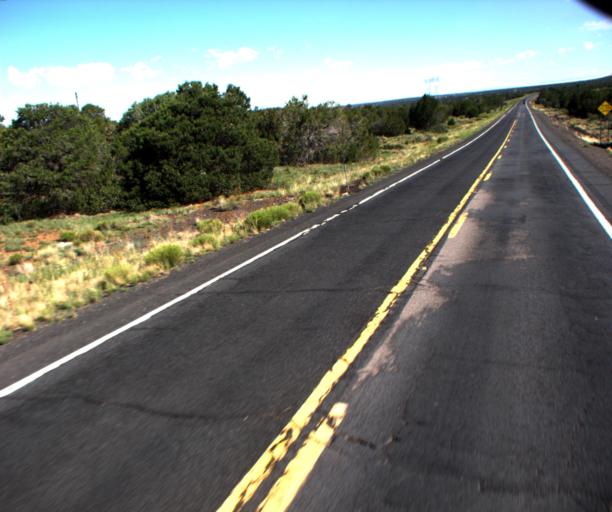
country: US
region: Arizona
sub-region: Coconino County
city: Williams
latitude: 35.4374
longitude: -112.1714
